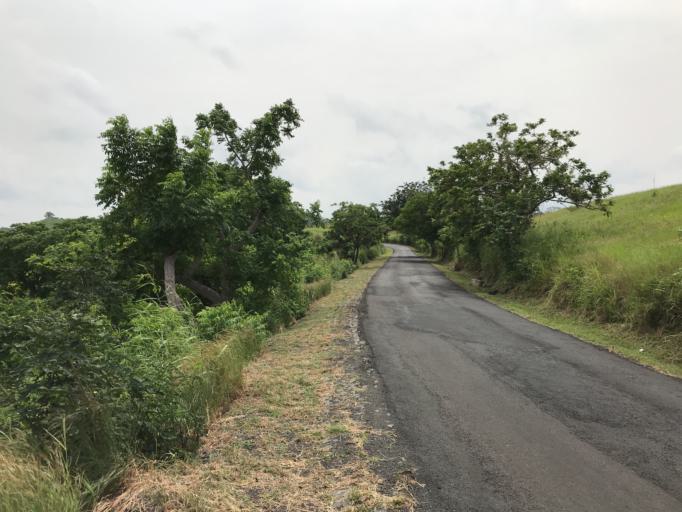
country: ST
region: Sao Tome Island
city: Sao Tome
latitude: 0.4002
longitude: 6.6196
